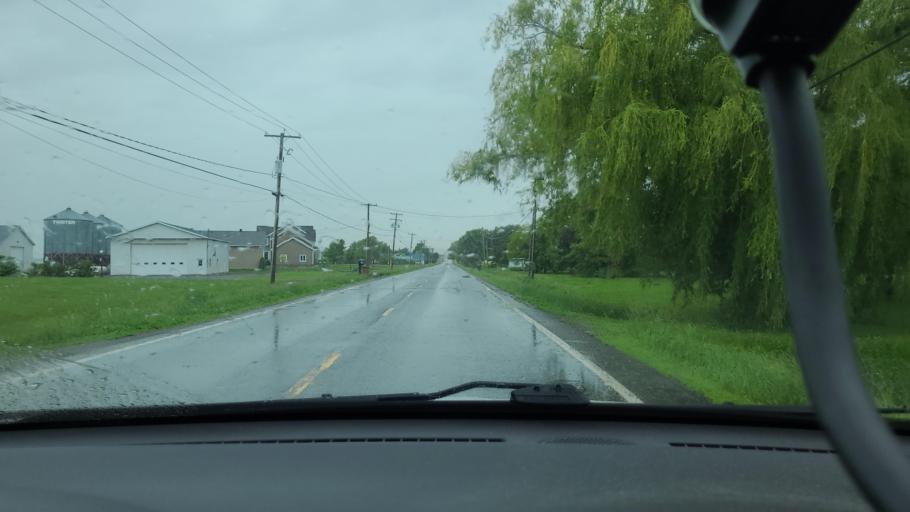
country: CA
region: Quebec
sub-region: Monteregie
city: Saint-Hyacinthe
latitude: 45.6170
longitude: -73.0511
